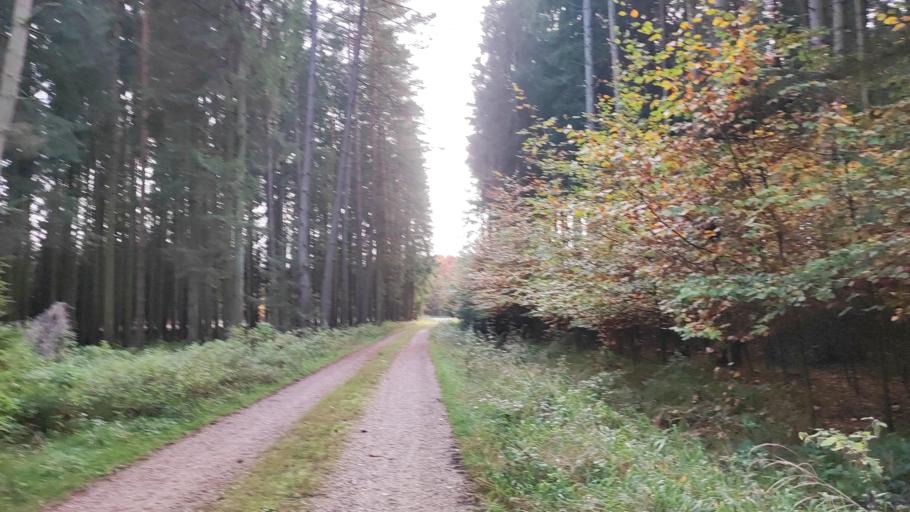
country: DE
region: Bavaria
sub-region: Swabia
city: Welden
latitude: 48.4383
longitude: 10.6293
